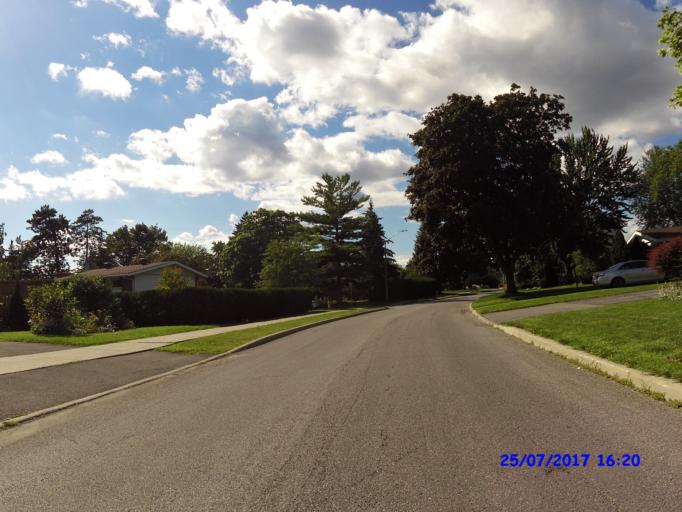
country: CA
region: Ontario
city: Ottawa
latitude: 45.3575
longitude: -75.7198
